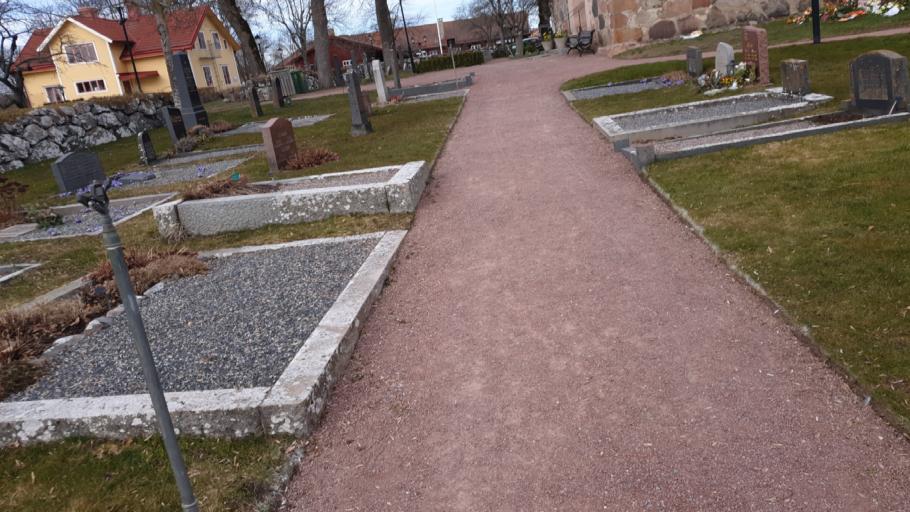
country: SE
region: Stockholm
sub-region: Vallentuna Kommun
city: Vallentuna
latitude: 59.5312
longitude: 18.0733
